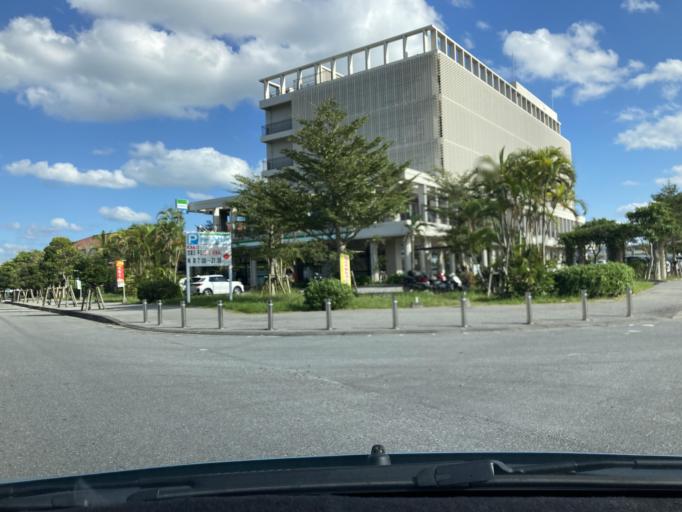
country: JP
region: Okinawa
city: Katsuren-haebaru
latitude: 26.3422
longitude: 127.8587
